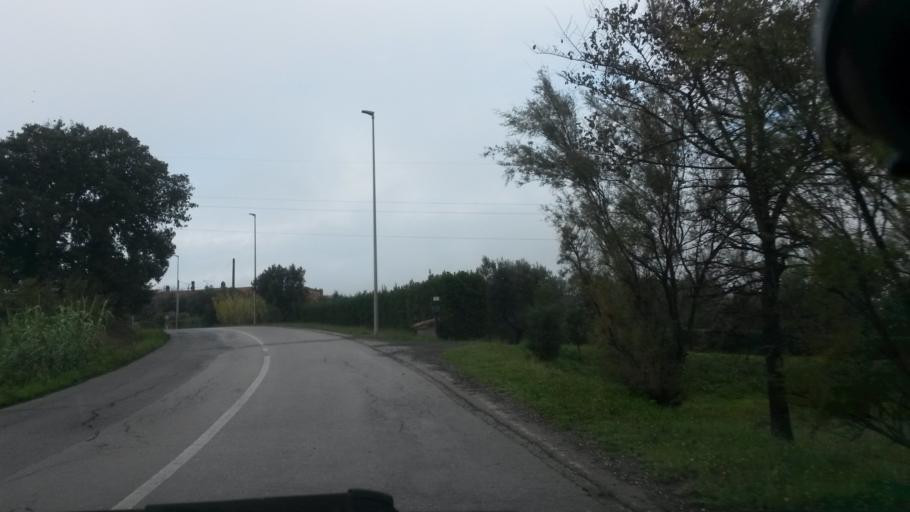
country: IT
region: Tuscany
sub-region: Provincia di Livorno
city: Rosignano Marittimo
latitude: 43.4168
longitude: 10.4623
